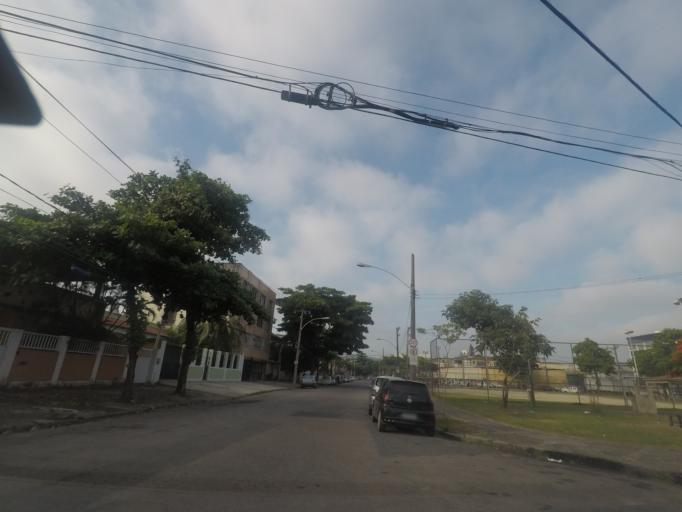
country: BR
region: Rio de Janeiro
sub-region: Duque De Caxias
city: Duque de Caxias
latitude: -22.8366
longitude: -43.2636
